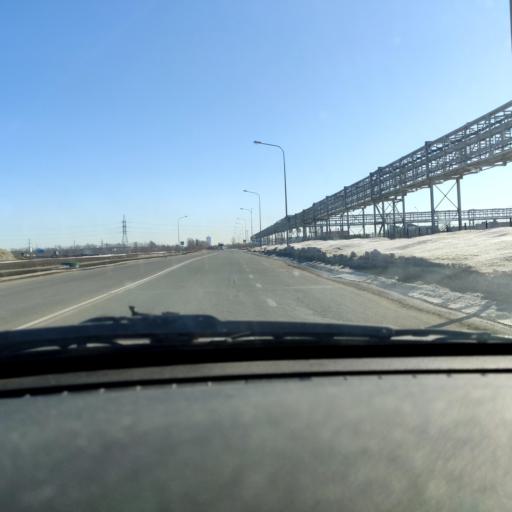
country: RU
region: Samara
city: Podstepki
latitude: 53.5596
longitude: 49.1977
